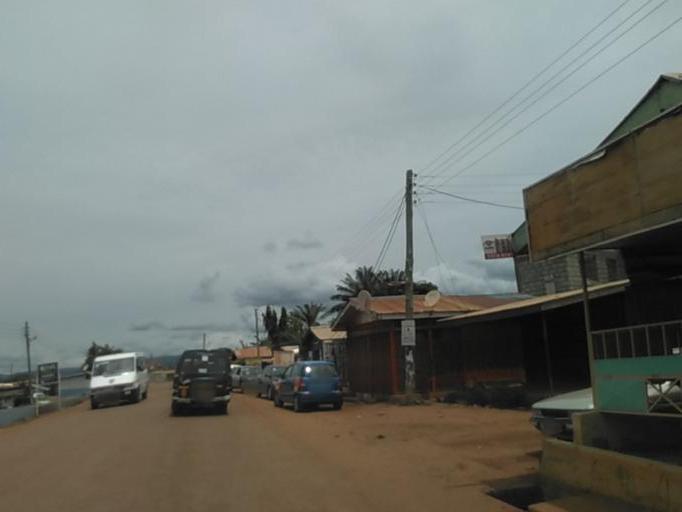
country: GH
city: Akropong
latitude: 6.1206
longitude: -0.0033
